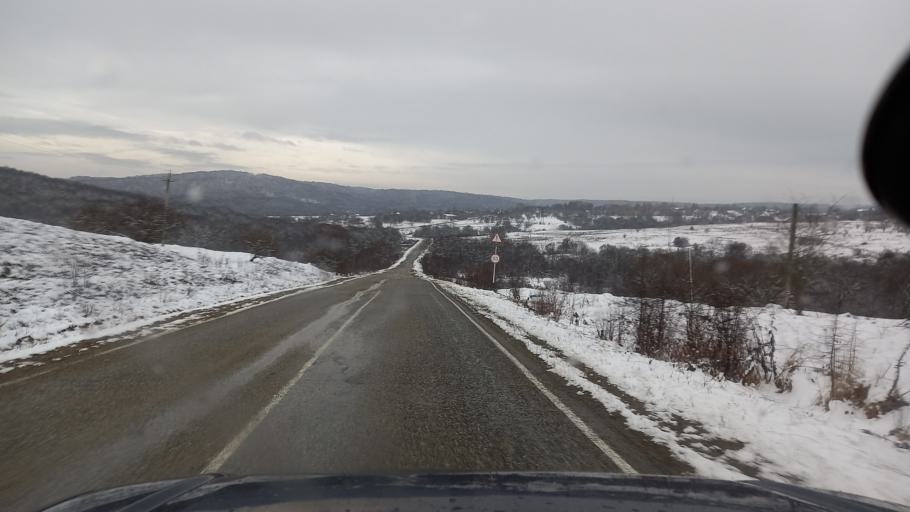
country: RU
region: Adygeya
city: Abadzekhskaya
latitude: 44.3593
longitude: 40.3940
